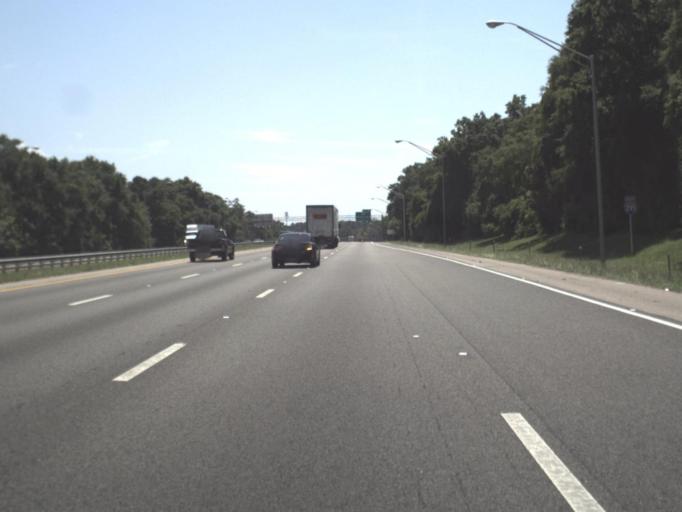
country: US
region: Florida
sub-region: Clay County
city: Bellair-Meadowbrook Terrace
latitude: 30.2909
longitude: -81.7715
